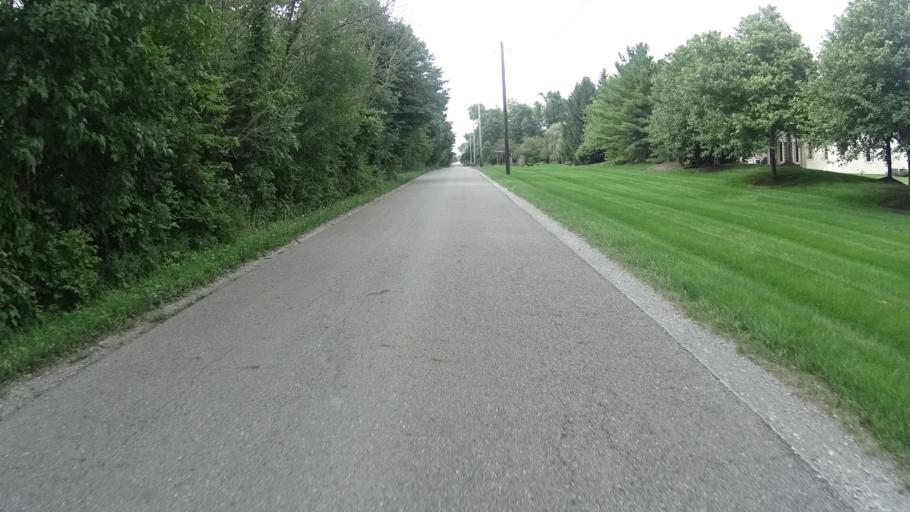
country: US
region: Indiana
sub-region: Madison County
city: Pendleton
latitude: 40.0060
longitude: -85.7870
